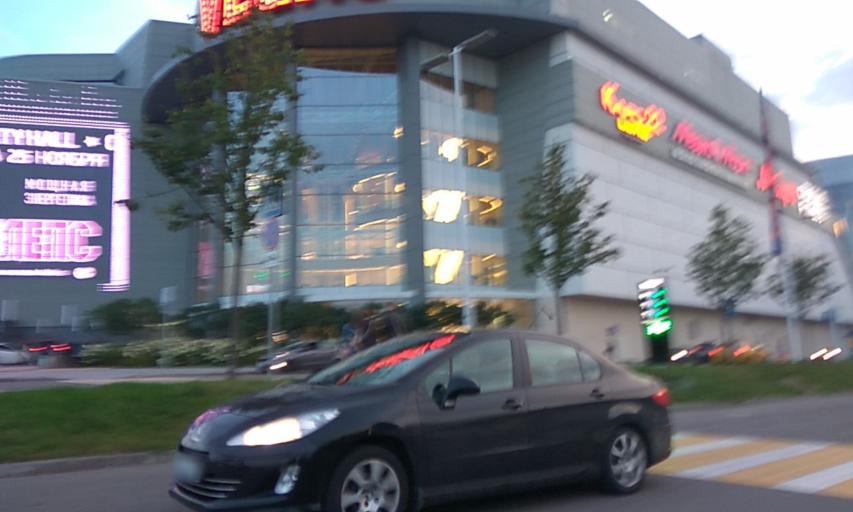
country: RU
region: Moscow
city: Strogino
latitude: 55.8215
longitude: 37.3904
